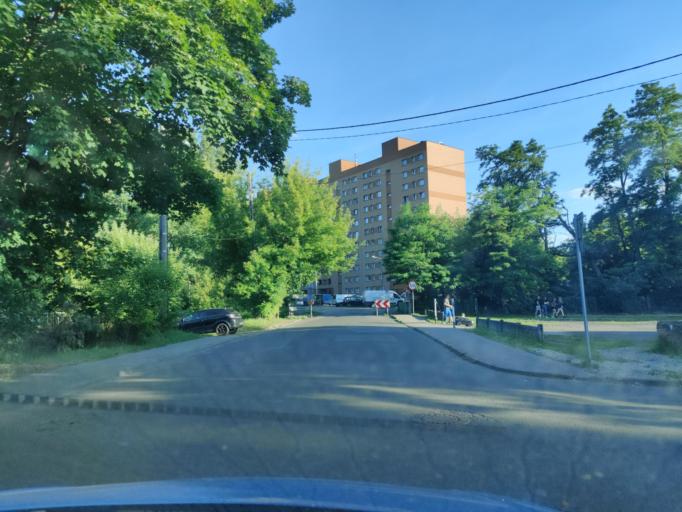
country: PL
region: Silesian Voivodeship
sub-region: Sosnowiec
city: Sosnowiec
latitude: 50.2532
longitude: 19.1352
